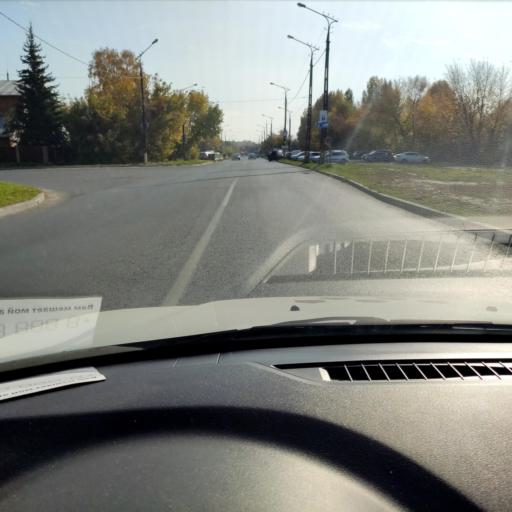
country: RU
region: Samara
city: Tol'yatti
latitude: 53.5149
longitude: 49.3955
